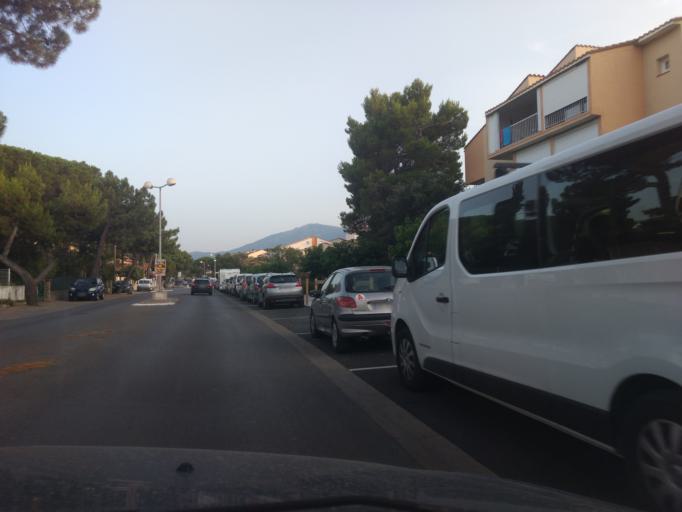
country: FR
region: Languedoc-Roussillon
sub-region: Departement des Pyrenees-Orientales
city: Argelers
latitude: 42.5586
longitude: 3.0414
